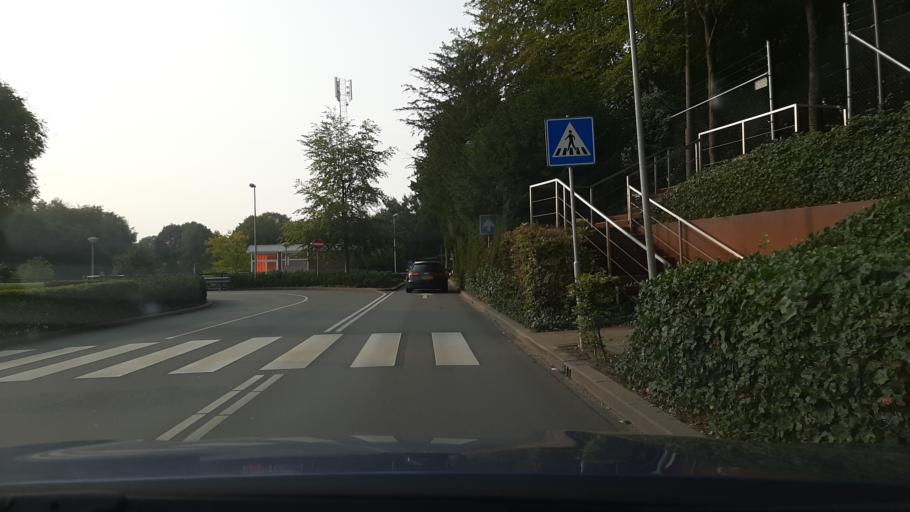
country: NL
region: Gelderland
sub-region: Gemeente Arnhem
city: Burgemeesterswijk
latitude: 52.0001
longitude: 5.9077
